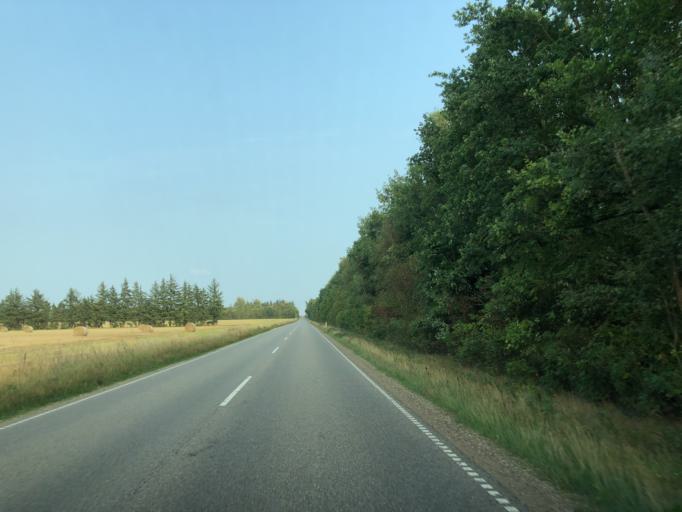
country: DK
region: South Denmark
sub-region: Billund Kommune
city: Grindsted
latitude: 55.8280
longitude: 8.9703
